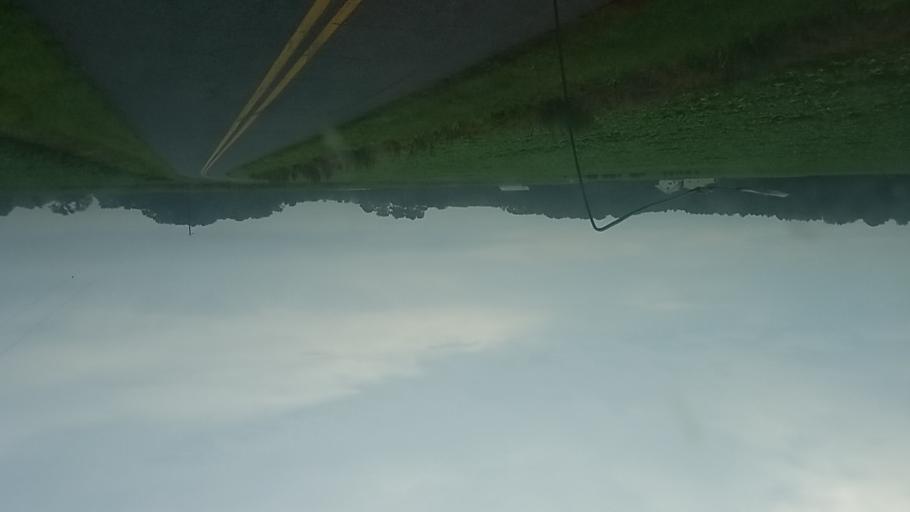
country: US
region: Maryland
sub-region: Wicomico County
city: Pittsville
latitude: 38.4232
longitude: -75.3183
